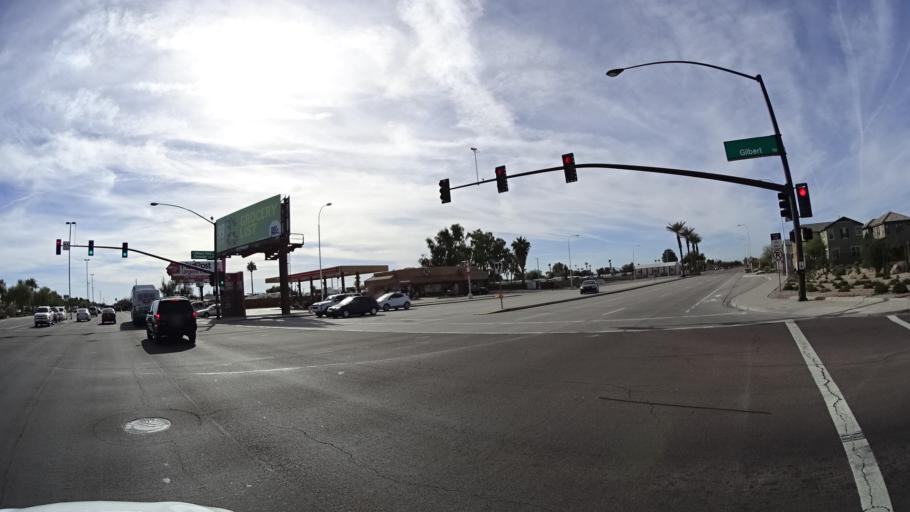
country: US
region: Arizona
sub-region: Maricopa County
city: Gilbert
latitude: 33.3067
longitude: -111.7899
